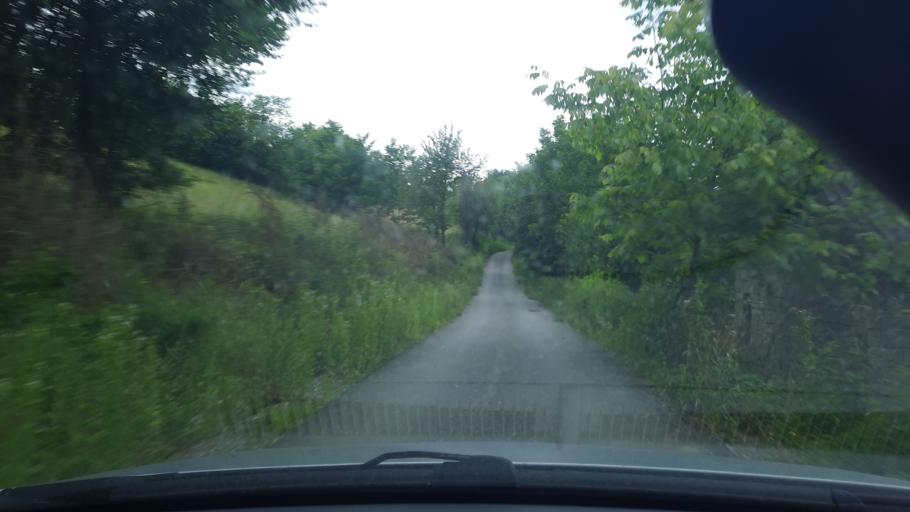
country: RS
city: Jarebice
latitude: 44.5152
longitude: 19.4783
